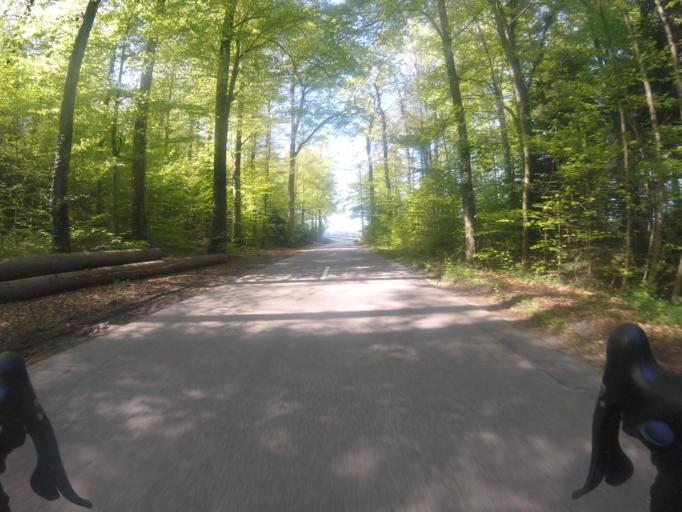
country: CH
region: Bern
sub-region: Bern-Mittelland District
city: Ferenbalm
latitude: 46.9522
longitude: 7.2287
